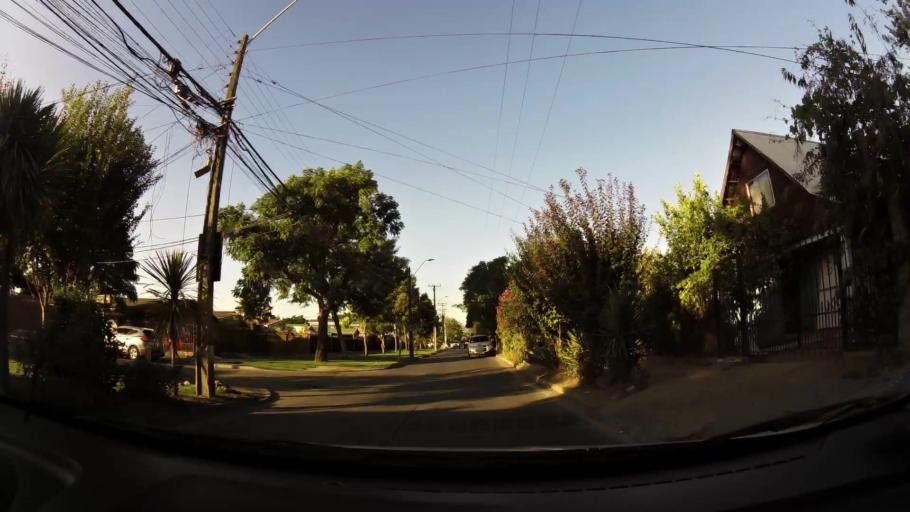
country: CL
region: Maule
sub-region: Provincia de Talca
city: Talca
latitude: -35.4466
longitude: -71.6726
